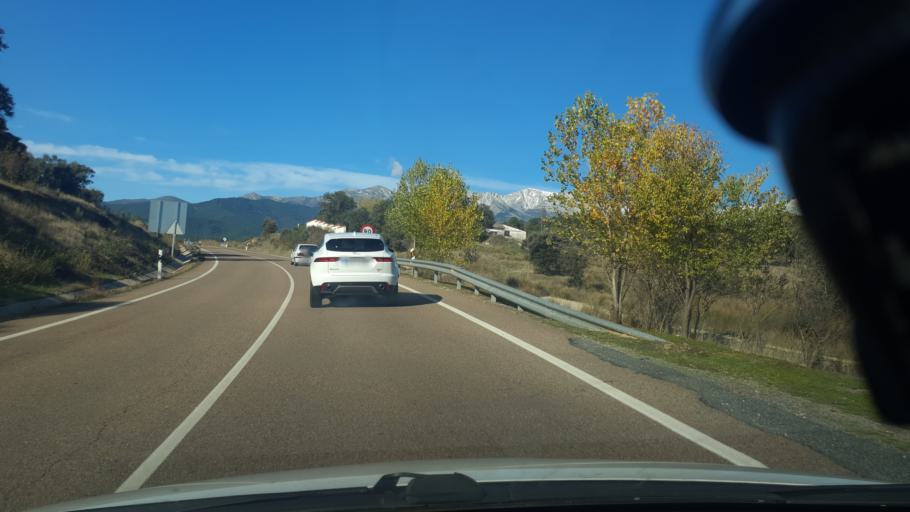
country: ES
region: Castille and Leon
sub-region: Provincia de Avila
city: Arenas de San Pedro
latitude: 40.1858
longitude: -5.0538
